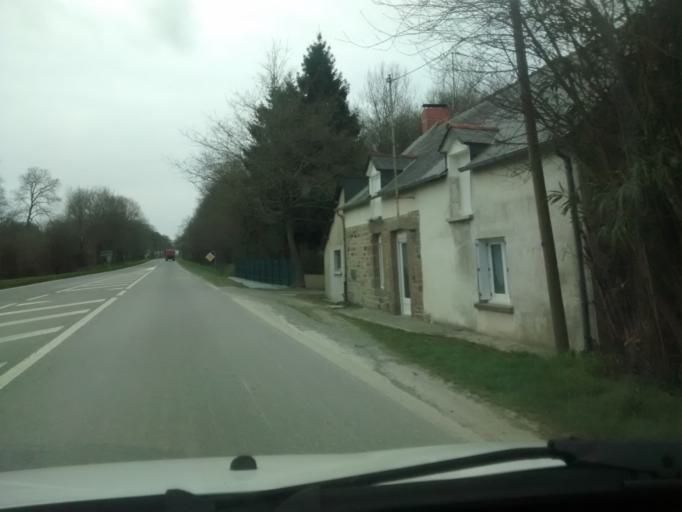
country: FR
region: Brittany
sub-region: Departement d'Ille-et-Vilaine
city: Sens-de-Bretagne
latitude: 48.3110
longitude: -1.5394
